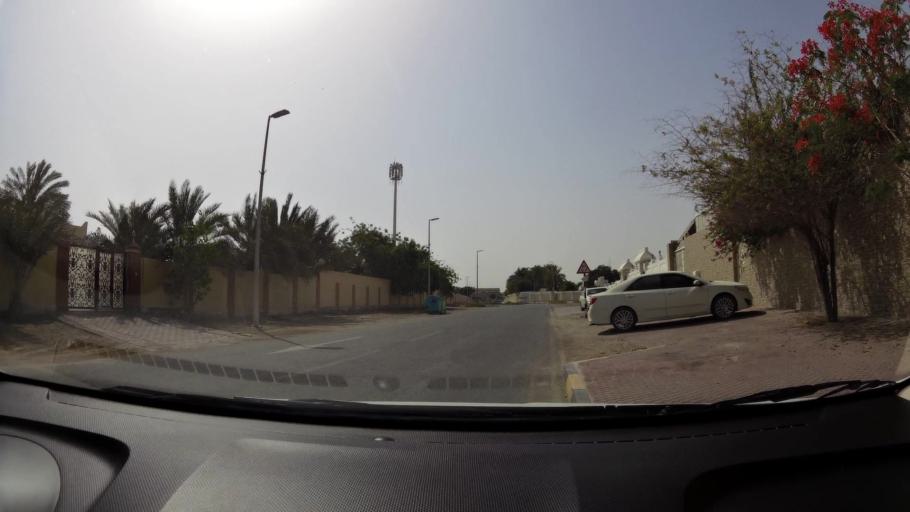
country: AE
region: Ash Shariqah
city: Sharjah
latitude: 25.3490
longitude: 55.4201
